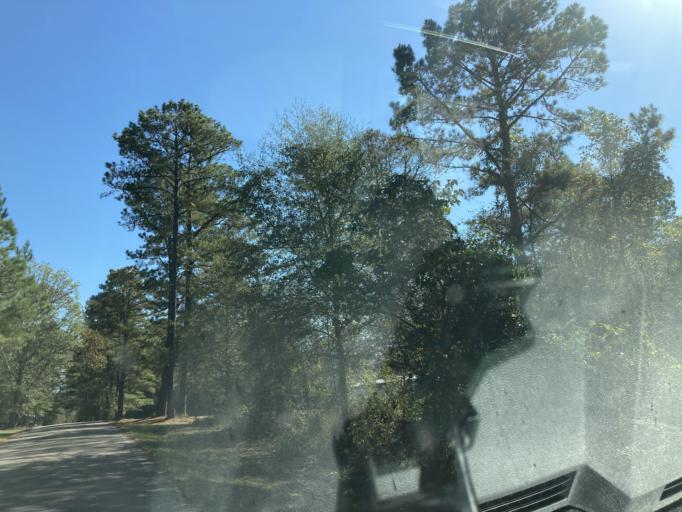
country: US
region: Mississippi
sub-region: Lamar County
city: Sumrall
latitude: 31.3169
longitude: -89.5153
